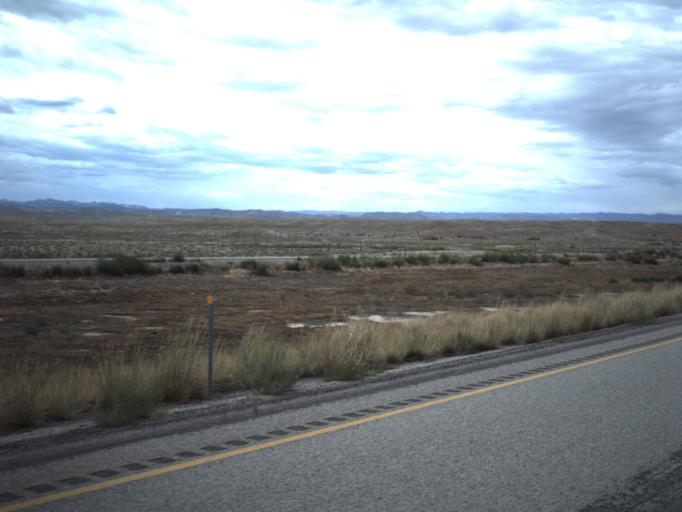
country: US
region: Utah
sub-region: Grand County
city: Moab
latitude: 39.0125
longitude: -109.3057
